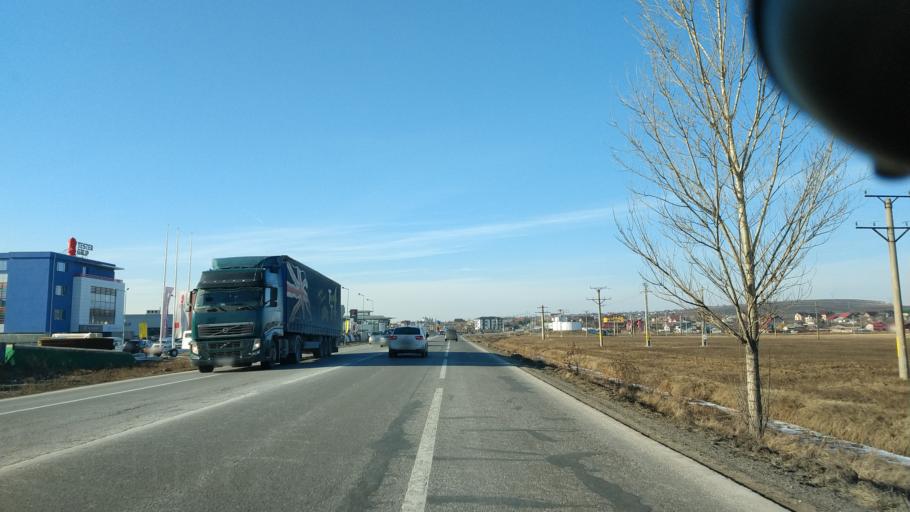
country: RO
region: Iasi
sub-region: Comuna Letcani
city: Letcani
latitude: 47.1893
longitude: 27.4340
